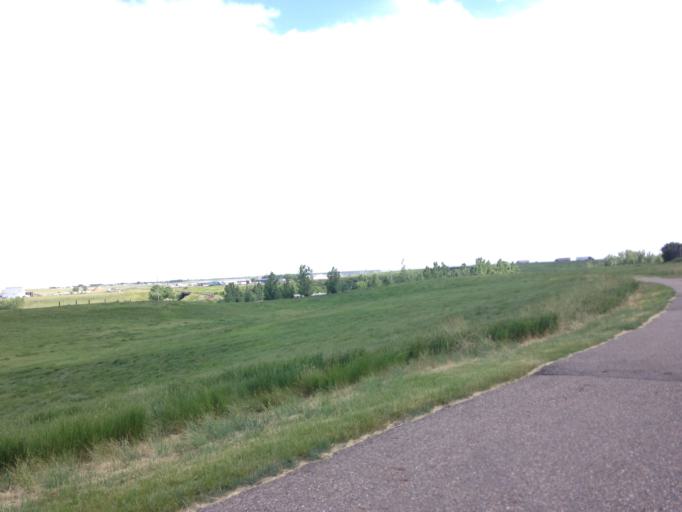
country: CA
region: Alberta
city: Medicine Hat
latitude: 49.9926
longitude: -110.6232
